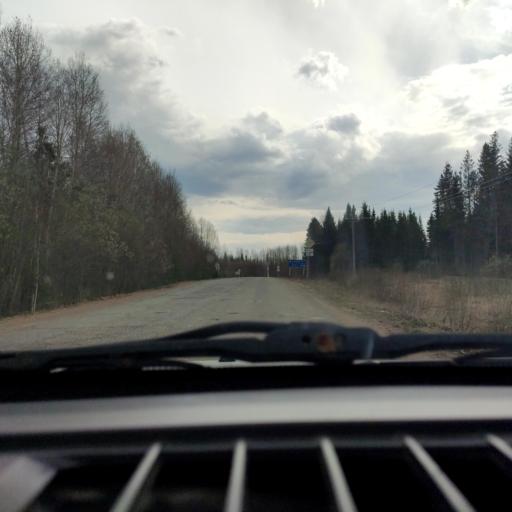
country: RU
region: Perm
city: Polazna
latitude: 58.3404
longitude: 56.1781
